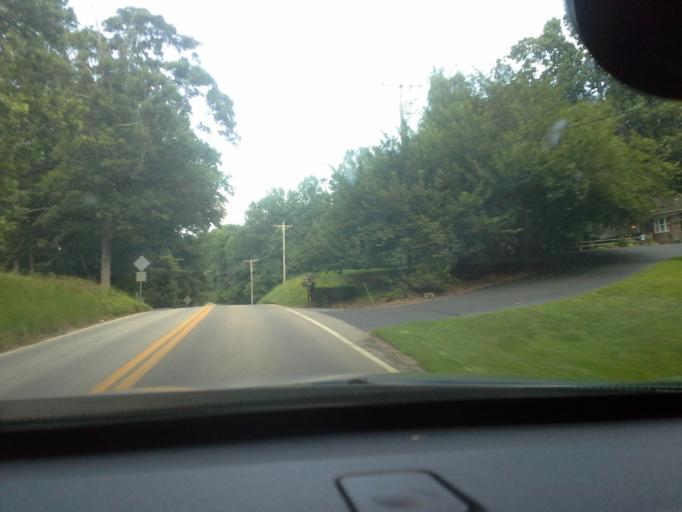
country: US
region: Maryland
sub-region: Calvert County
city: Prince Frederick
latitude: 38.5936
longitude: -76.5445
